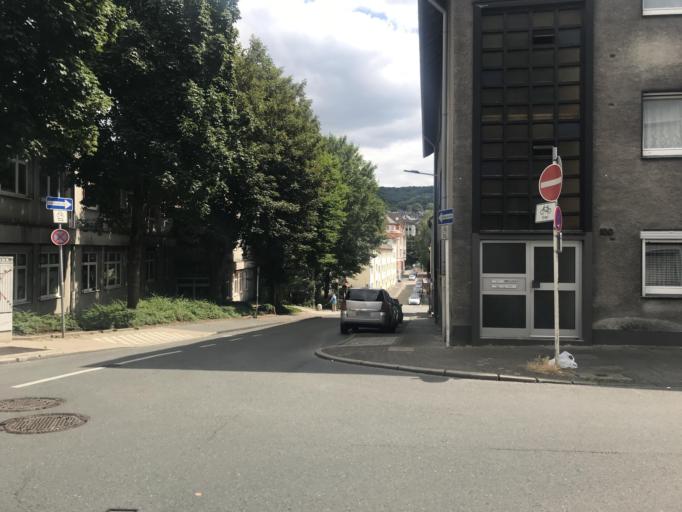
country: DE
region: North Rhine-Westphalia
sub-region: Regierungsbezirk Dusseldorf
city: Wuppertal
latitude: 51.2710
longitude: 7.1932
